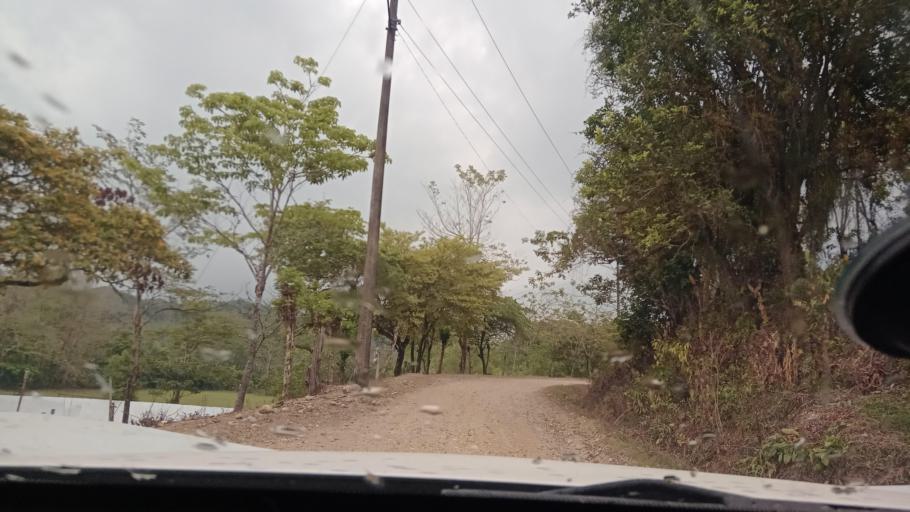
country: MX
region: Veracruz
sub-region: Uxpanapa
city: Poblado 10
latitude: 17.4517
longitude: -94.0925
